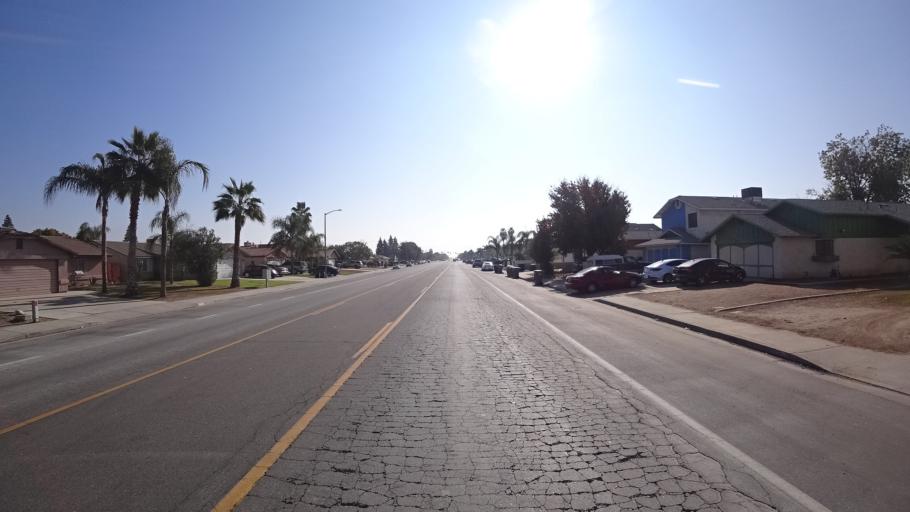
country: US
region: California
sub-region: Kern County
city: Greenfield
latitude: 35.2985
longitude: -119.0120
